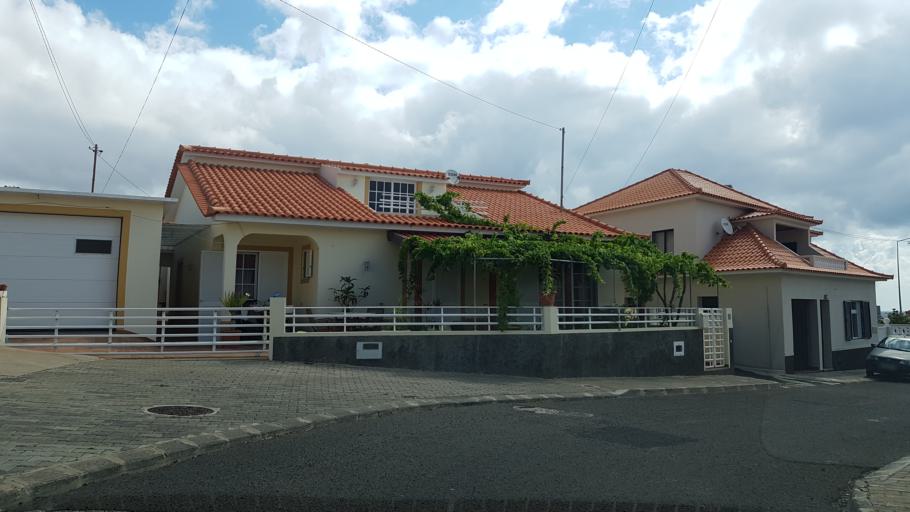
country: PT
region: Madeira
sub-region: Porto Santo
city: Vila de Porto Santo
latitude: 33.0359
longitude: -16.3711
